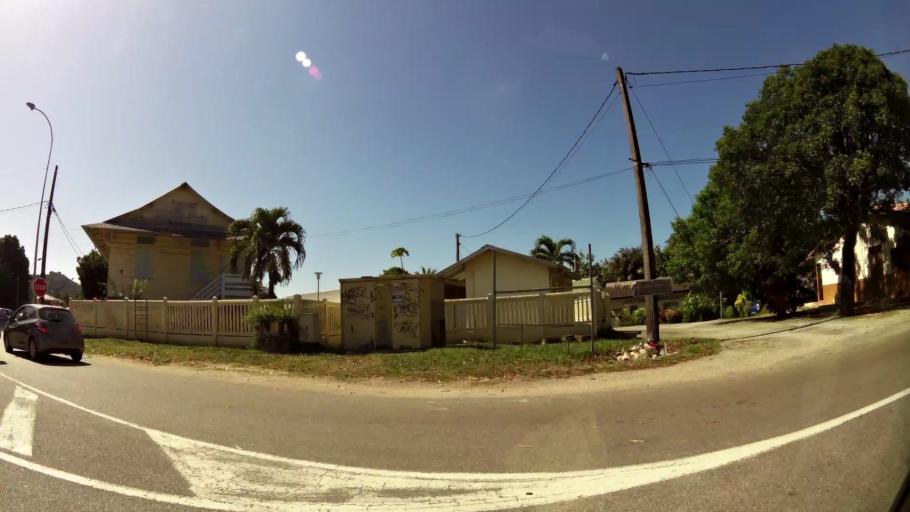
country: GF
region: Guyane
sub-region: Guyane
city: Remire-Montjoly
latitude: 4.9127
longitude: -52.2725
